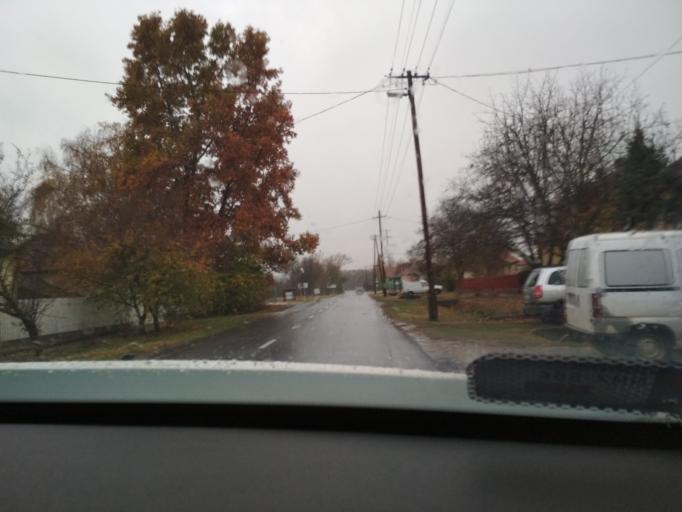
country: HU
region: Csongrad
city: Baks
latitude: 46.5411
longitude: 20.1019
